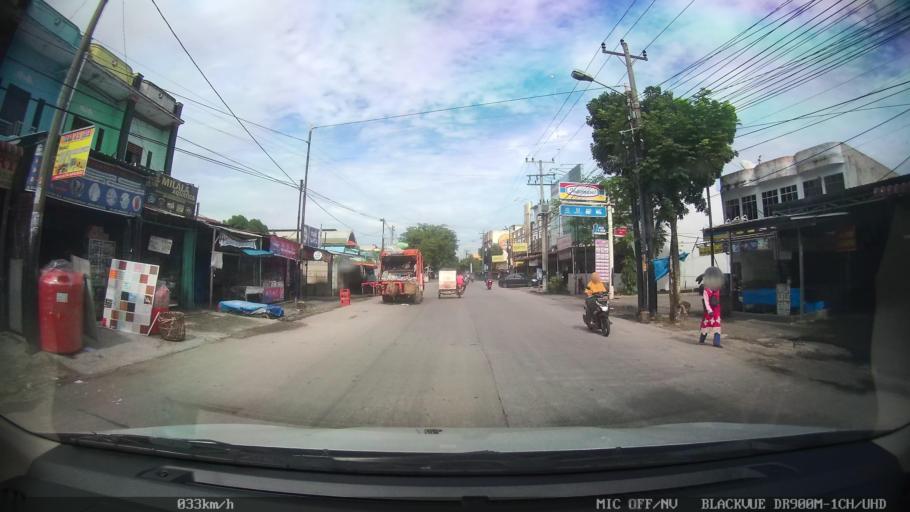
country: ID
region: North Sumatra
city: Sunggal
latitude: 3.6062
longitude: 98.6160
